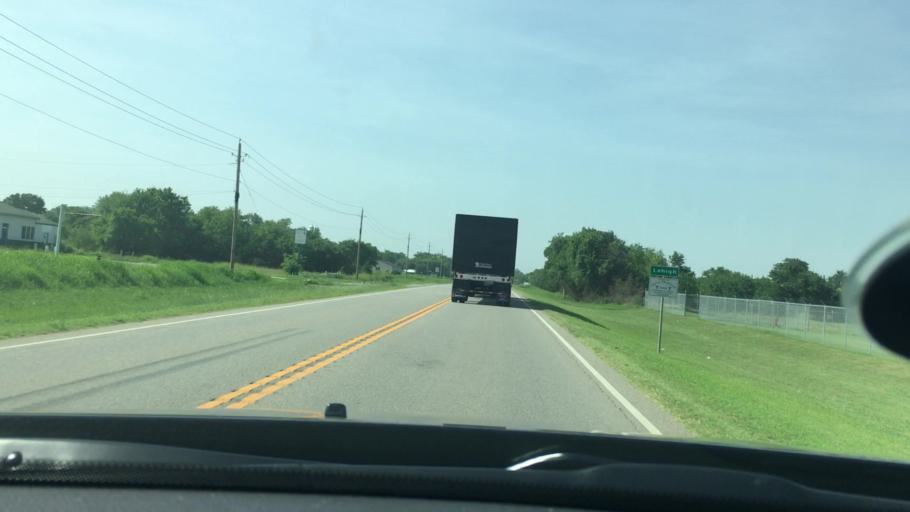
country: US
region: Oklahoma
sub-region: Coal County
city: Coalgate
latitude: 34.4781
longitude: -96.2181
